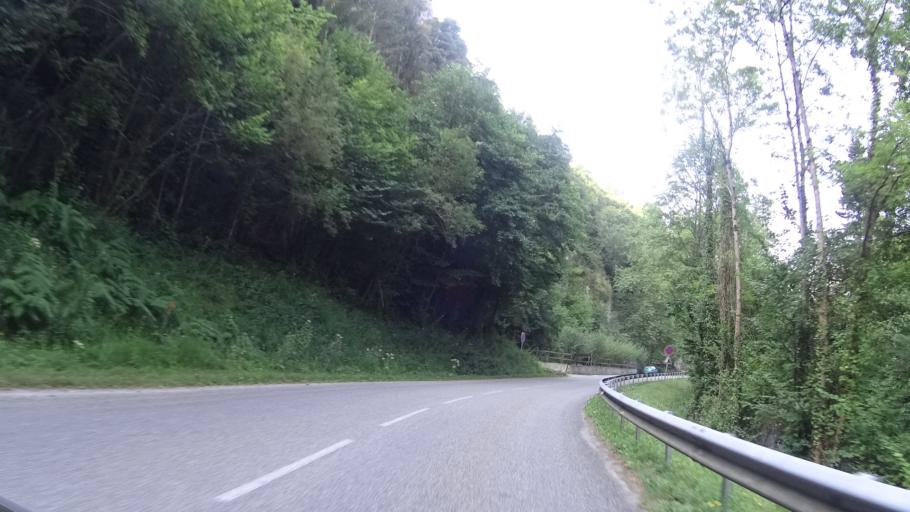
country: FR
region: Midi-Pyrenees
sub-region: Departement de l'Ariege
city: Belesta
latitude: 42.8935
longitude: 1.9277
